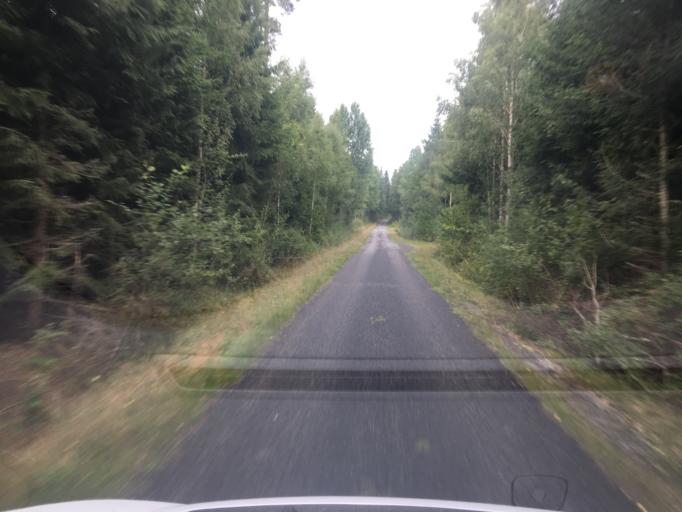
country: SE
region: Kronoberg
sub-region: Ljungby Kommun
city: Lagan
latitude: 56.9505
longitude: 14.0360
